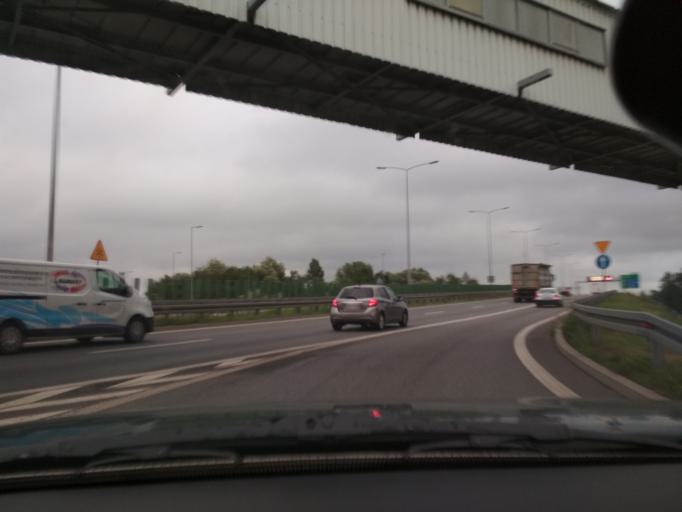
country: PL
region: Silesian Voivodeship
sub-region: Gliwice
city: Gliwice
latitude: 50.2838
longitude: 18.7112
